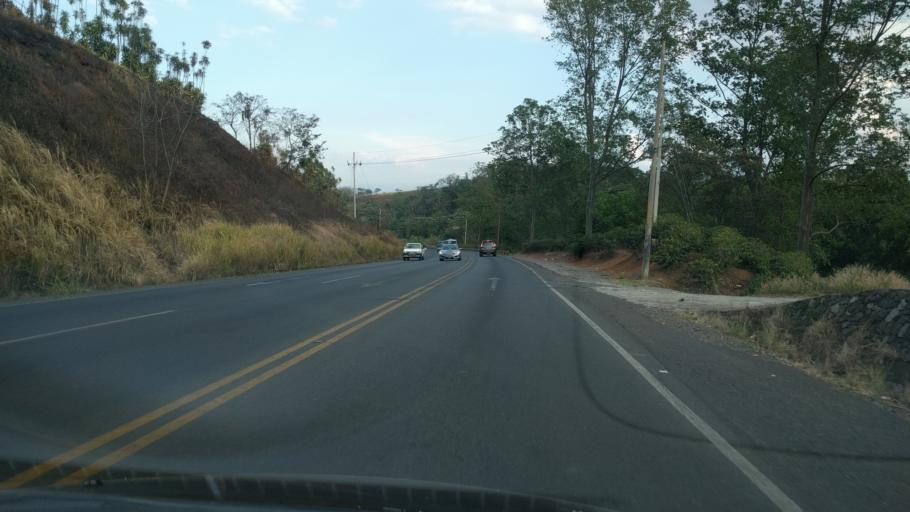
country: CR
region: Alajuela
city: Naranjo
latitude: 10.0677
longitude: -84.3679
